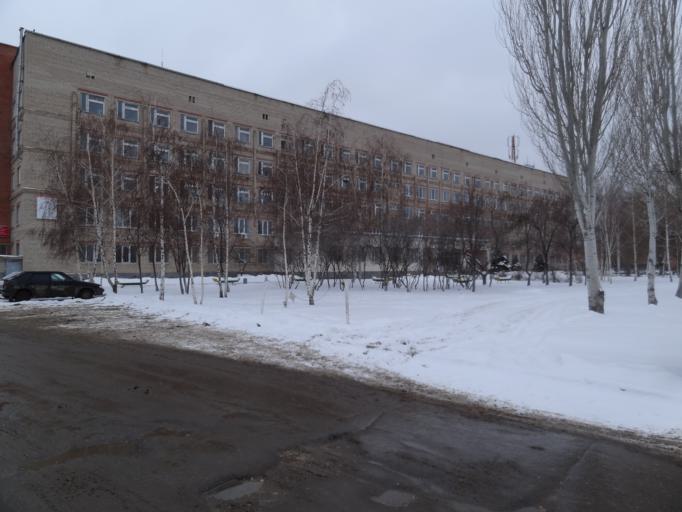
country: RU
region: Saratov
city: Engel's
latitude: 51.4963
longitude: 46.1526
